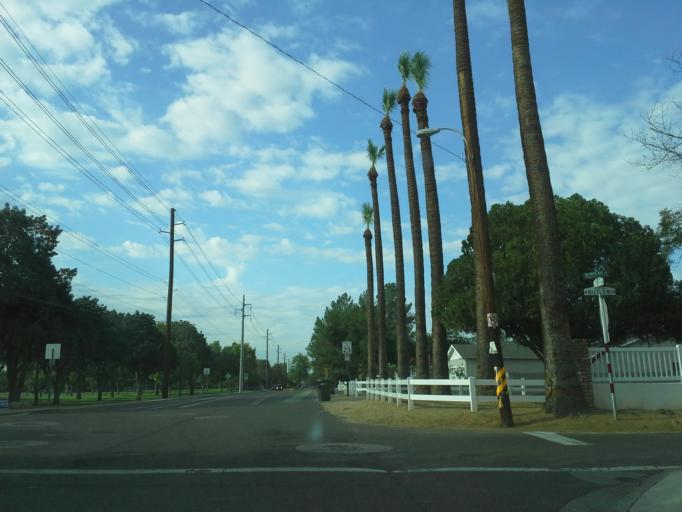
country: US
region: Arizona
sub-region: Maricopa County
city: Glendale
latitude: 33.5605
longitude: -112.0913
